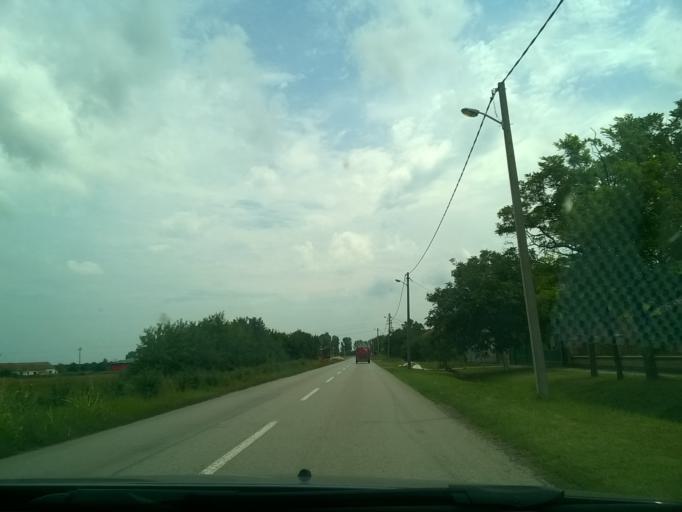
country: RS
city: Hajducica
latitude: 45.2545
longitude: 20.9671
